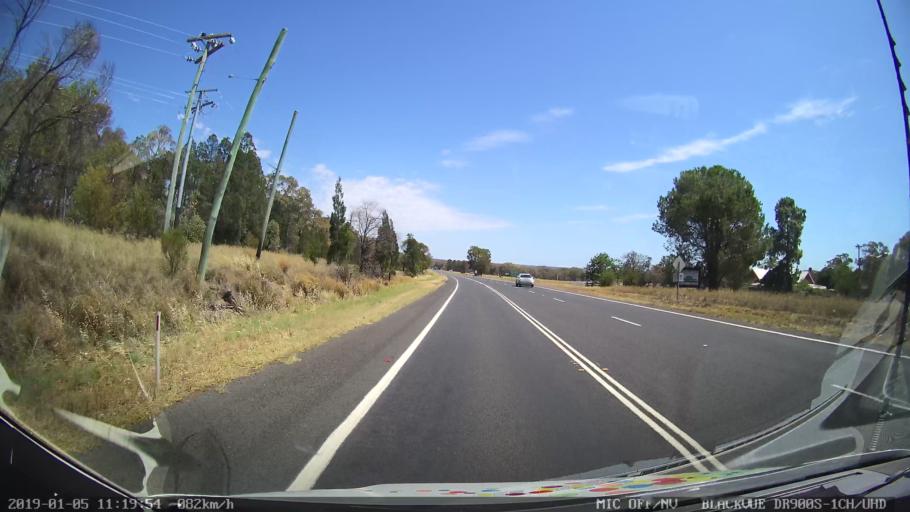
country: AU
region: New South Wales
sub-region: Warrumbungle Shire
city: Coonabarabran
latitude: -31.2986
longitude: 149.2936
